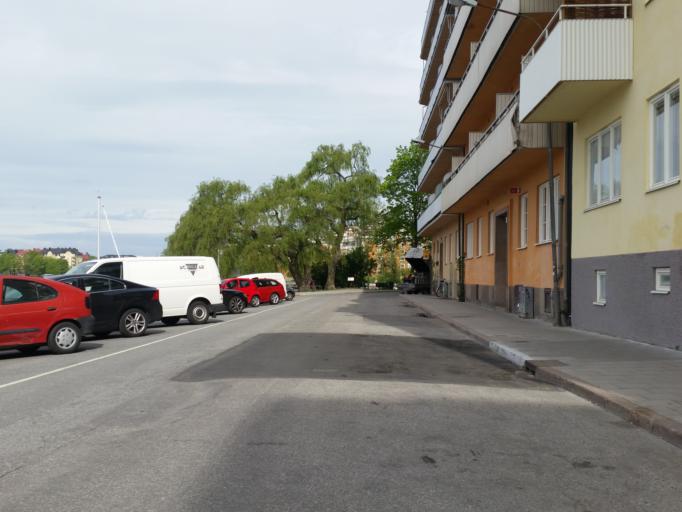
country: SE
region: Stockholm
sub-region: Stockholms Kommun
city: Arsta
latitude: 59.3157
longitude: 18.0279
